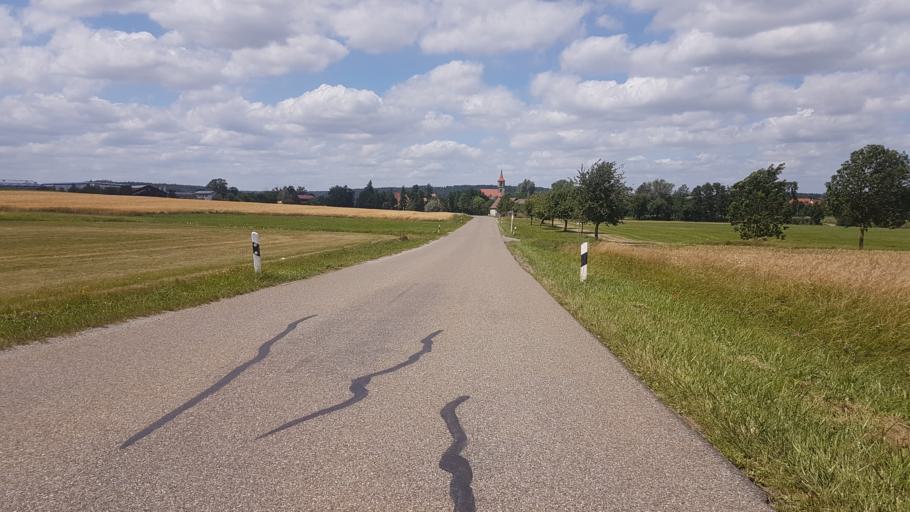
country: DE
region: Bavaria
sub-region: Regierungsbezirk Mittelfranken
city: Geslau
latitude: 49.3613
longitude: 10.3136
